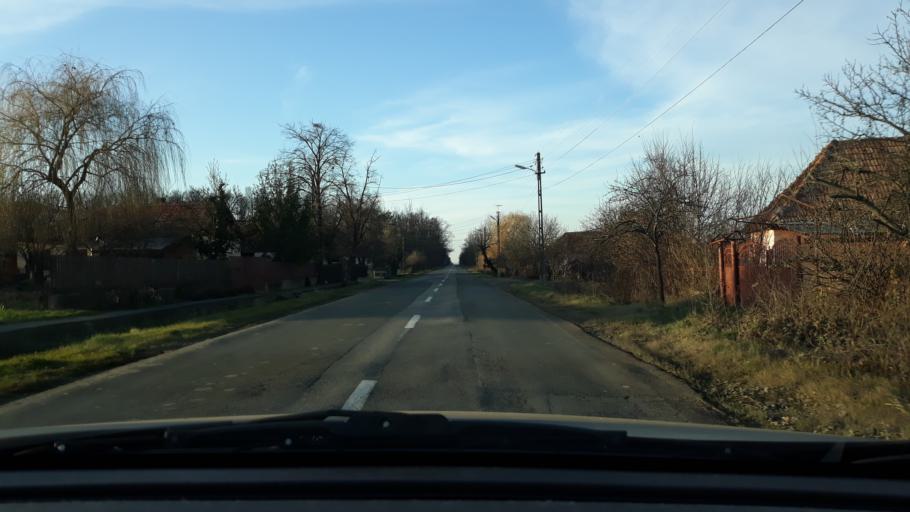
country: RO
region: Bihor
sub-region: Comuna Balc
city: Balc
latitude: 47.2796
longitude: 22.4764
